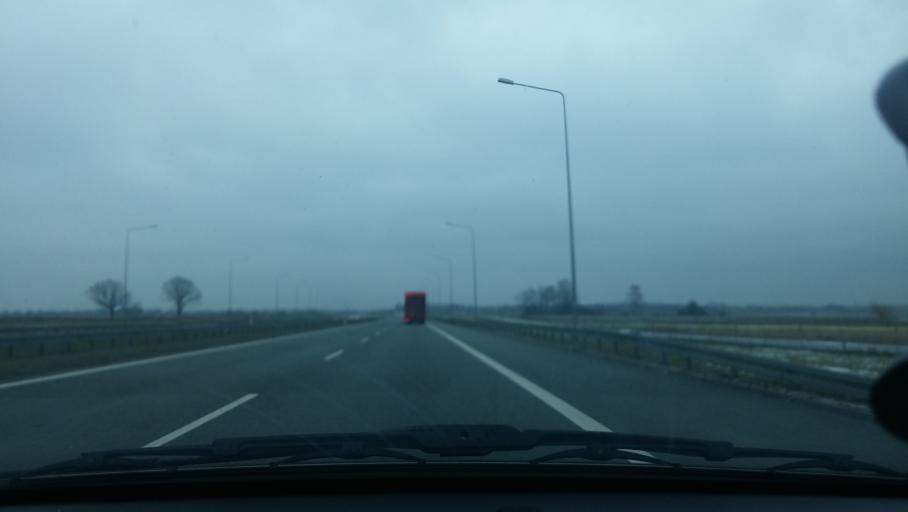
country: PL
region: Masovian Voivodeship
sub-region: Powiat minski
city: Jakubow
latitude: 52.2033
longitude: 21.7065
